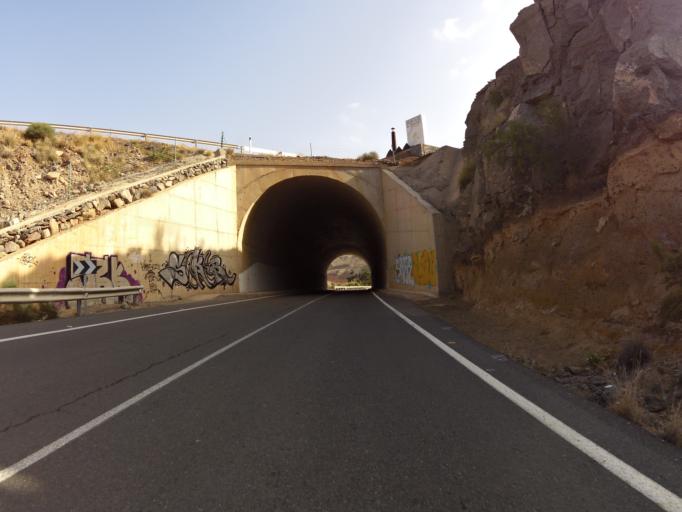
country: ES
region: Canary Islands
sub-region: Provincia de Las Palmas
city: Puerto Rico
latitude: 27.7653
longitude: -15.6679
